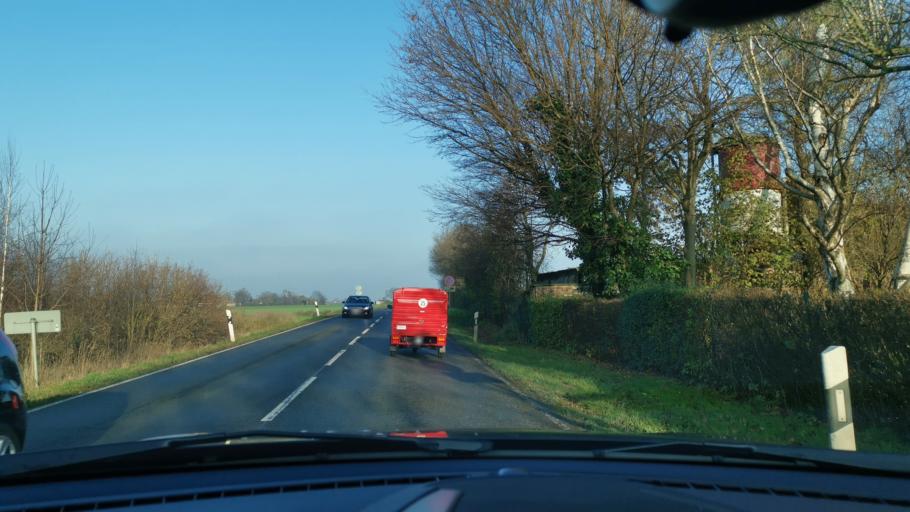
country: DE
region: North Rhine-Westphalia
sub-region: Regierungsbezirk Dusseldorf
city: Neubrueck
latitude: 51.1280
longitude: 6.6742
